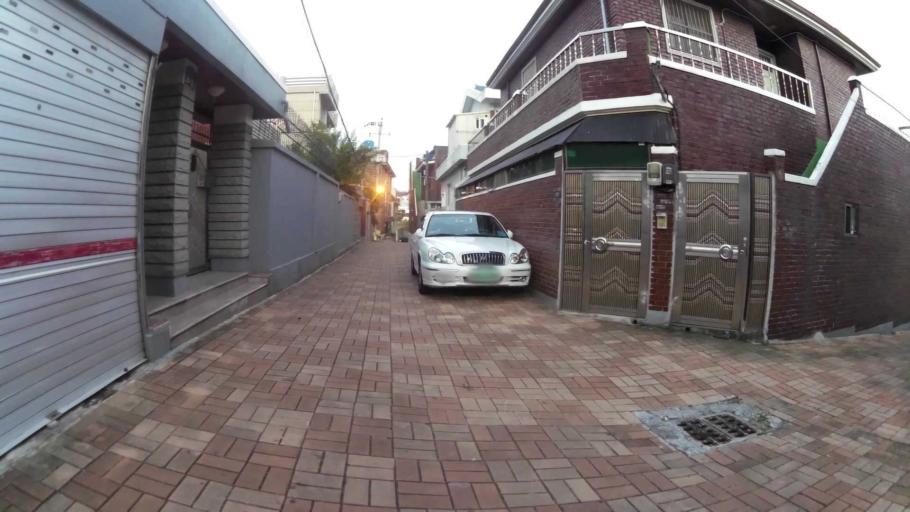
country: KR
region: Daegu
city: Daegu
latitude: 35.8615
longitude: 128.6429
